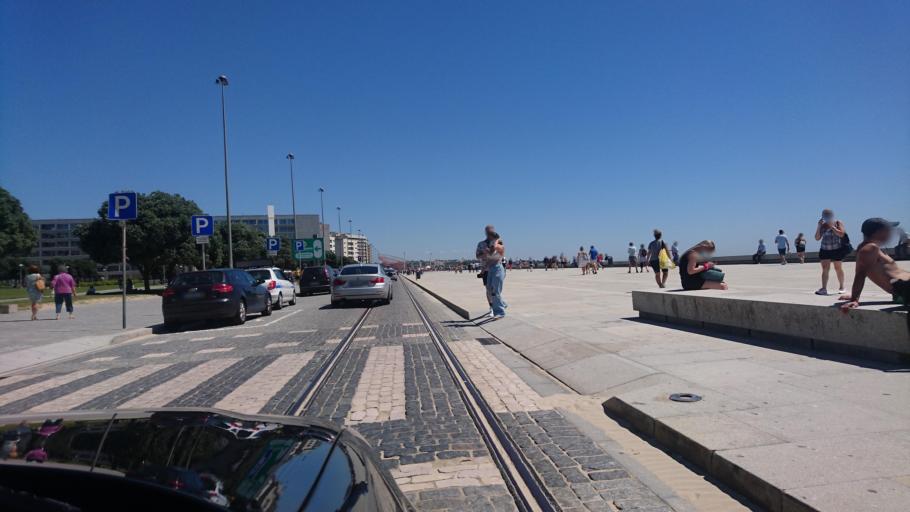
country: PT
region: Porto
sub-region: Matosinhos
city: Matosinhos
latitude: 41.1795
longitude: -8.6936
